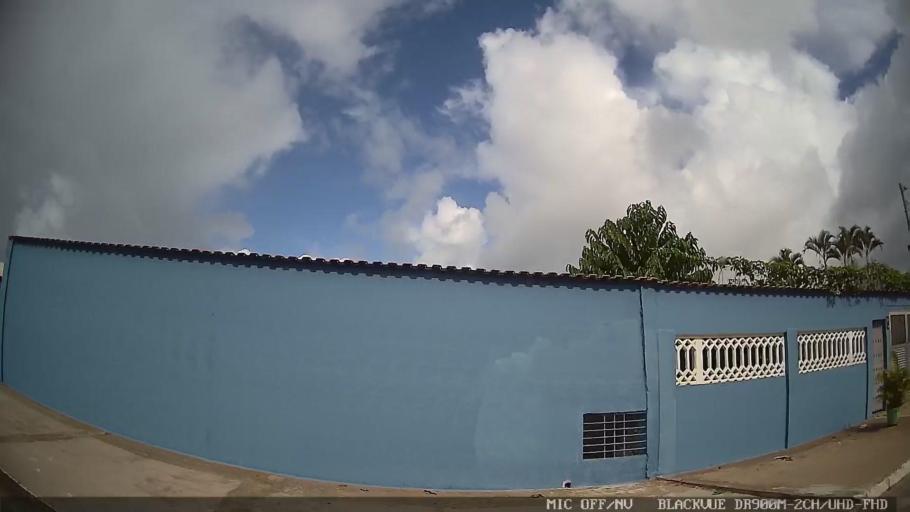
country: BR
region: Sao Paulo
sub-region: Itanhaem
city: Itanhaem
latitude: -24.2375
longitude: -46.8858
